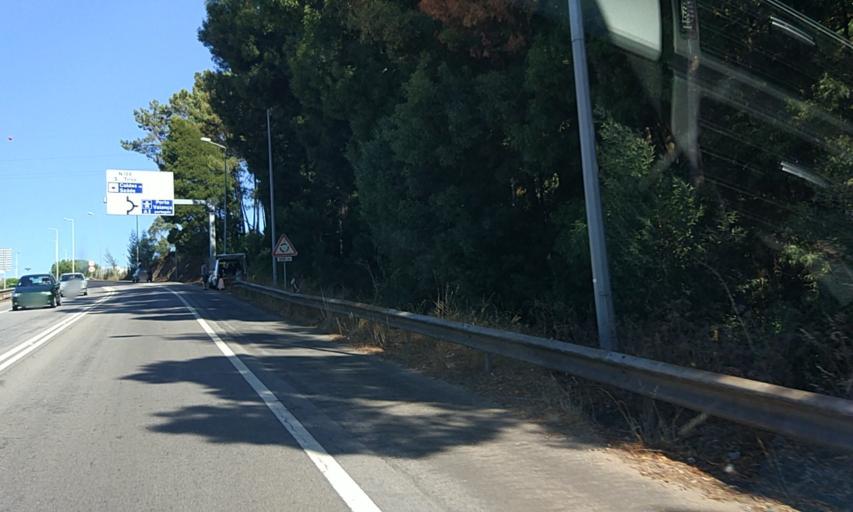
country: PT
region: Porto
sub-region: Santo Tirso
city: Santo Tirso
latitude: 41.3393
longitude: -8.5118
